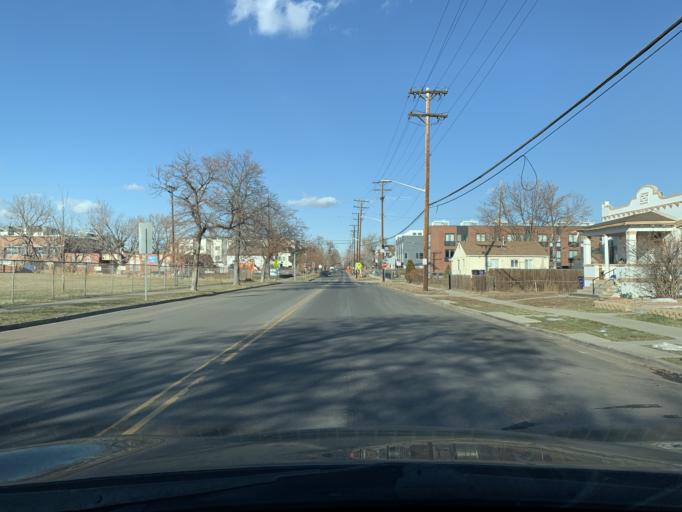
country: US
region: Colorado
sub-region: Jefferson County
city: Edgewater
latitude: 39.7419
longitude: -105.0299
